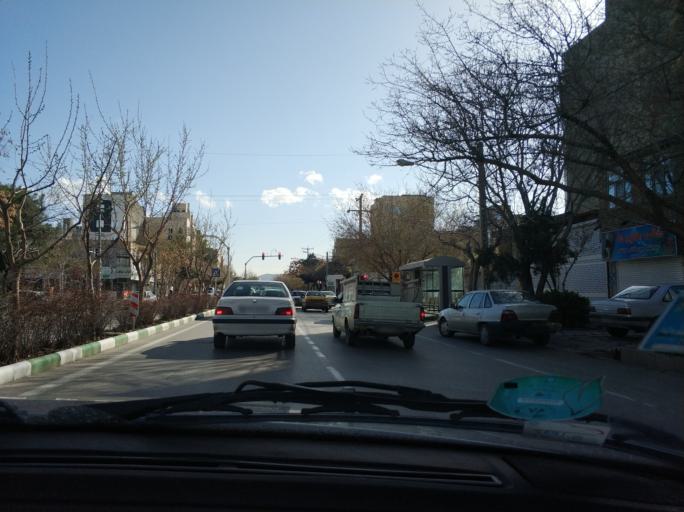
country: IR
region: Razavi Khorasan
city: Mashhad
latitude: 36.3148
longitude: 59.6265
